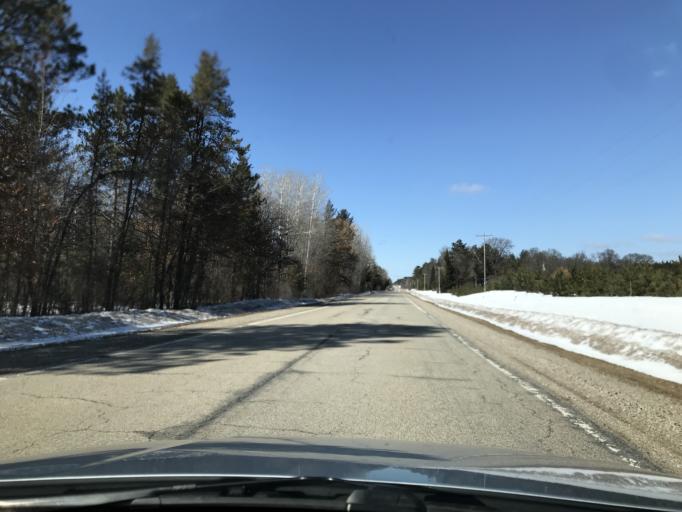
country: US
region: Wisconsin
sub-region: Marinette County
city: Niagara
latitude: 45.3627
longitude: -88.1006
